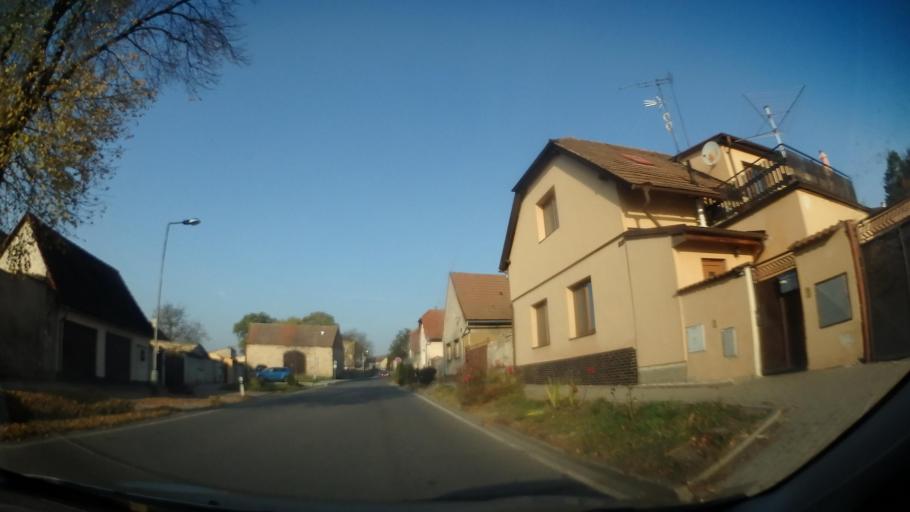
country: CZ
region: Central Bohemia
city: Jirny
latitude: 50.1139
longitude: 14.7021
